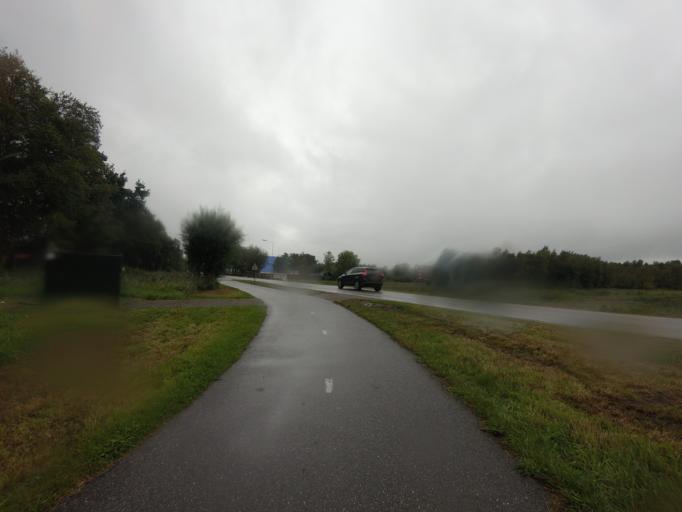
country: NL
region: Friesland
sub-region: Gemeente Tytsjerksteradiel
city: Garyp
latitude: 53.1373
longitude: 5.9496
